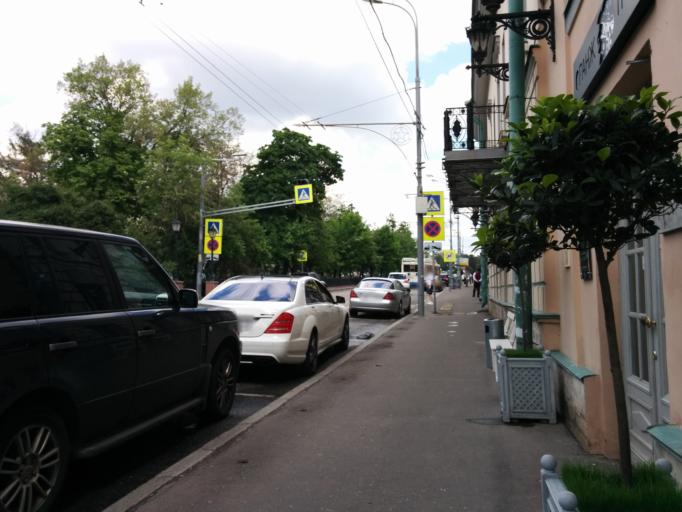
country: RU
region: Moscow
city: Moscow
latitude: 55.7628
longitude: 37.6040
